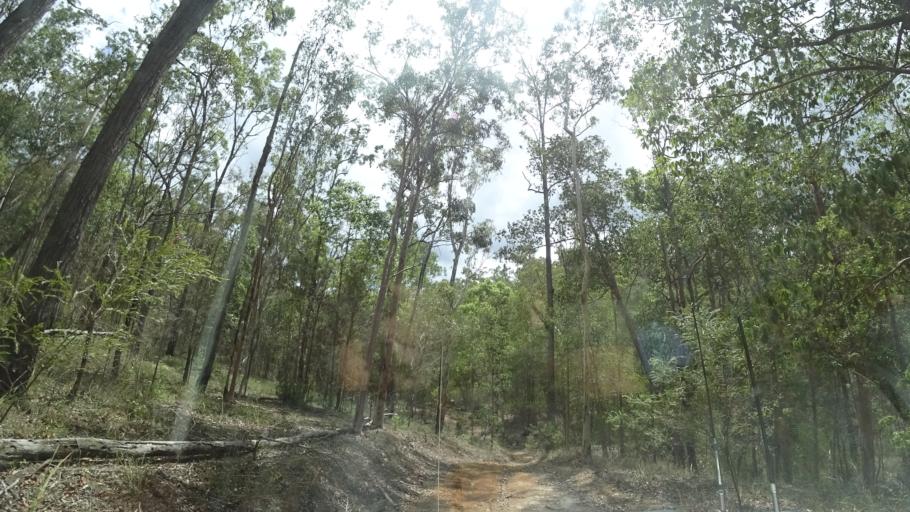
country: AU
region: Queensland
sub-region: Moreton Bay
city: Highvale
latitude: -27.4328
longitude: 152.7508
